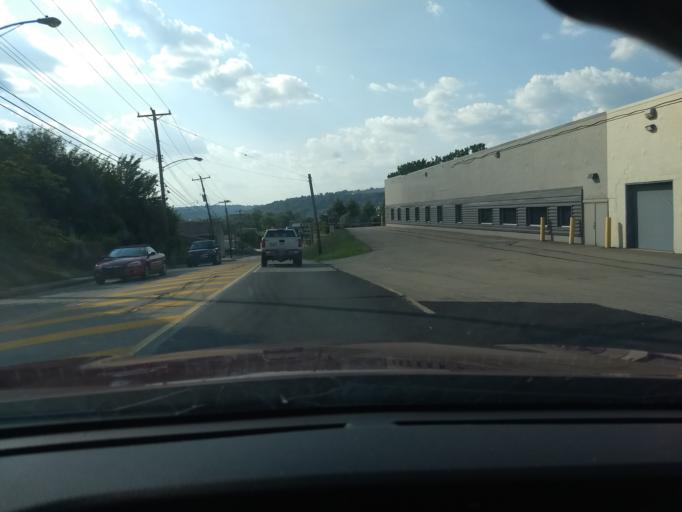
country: US
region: Pennsylvania
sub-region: Allegheny County
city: Versailles
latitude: 40.3218
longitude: -79.8371
